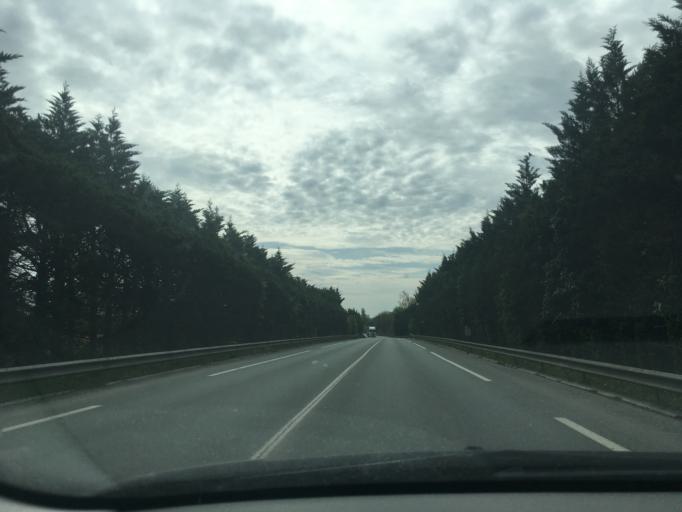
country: FR
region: Poitou-Charentes
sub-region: Departement de la Charente
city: Cognac
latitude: 45.6910
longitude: -0.3459
